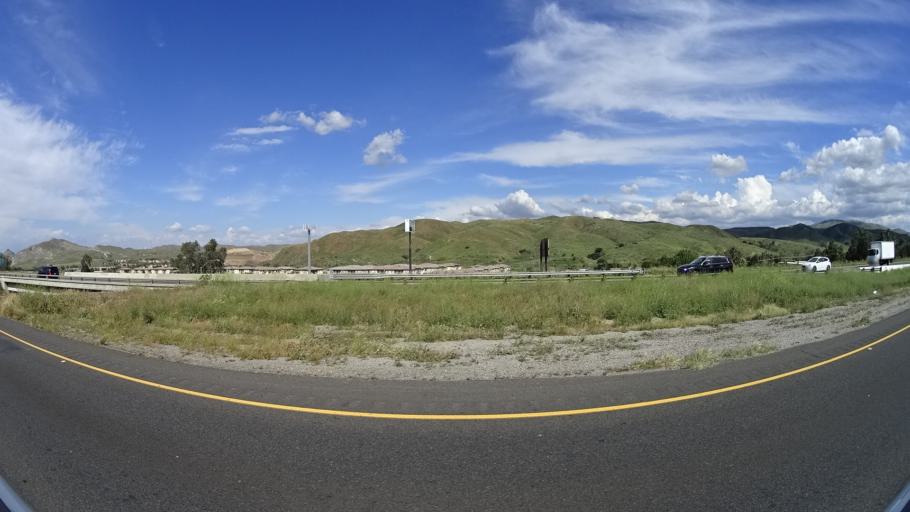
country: US
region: California
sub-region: Riverside County
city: El Cerrito
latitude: 33.8067
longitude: -117.5075
